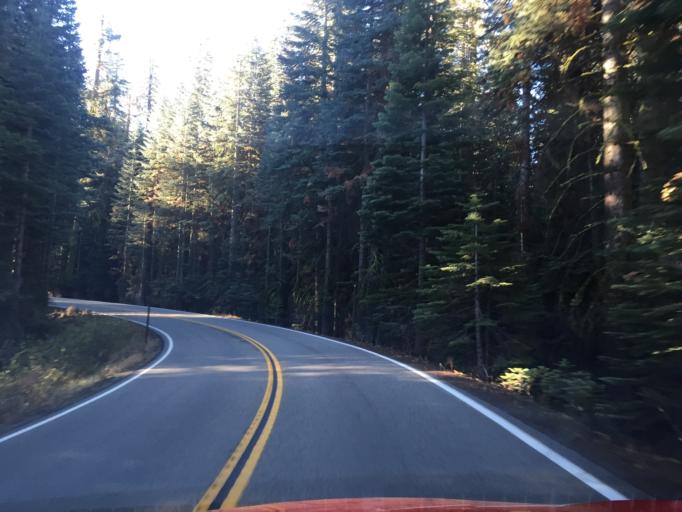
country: US
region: California
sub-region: Mariposa County
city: Yosemite Valley
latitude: 37.6711
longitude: -119.6777
